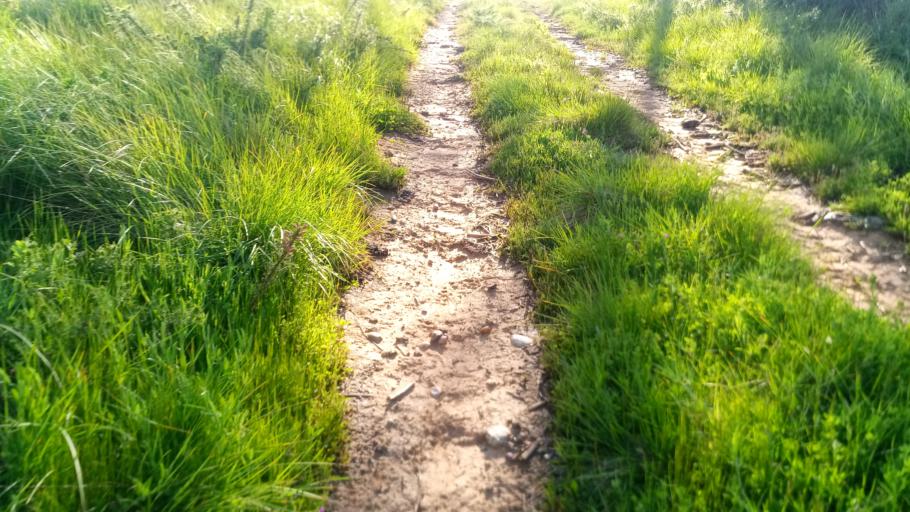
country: PT
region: Leiria
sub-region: Caldas da Rainha
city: Caldas da Rainha
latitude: 39.4627
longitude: -9.1996
